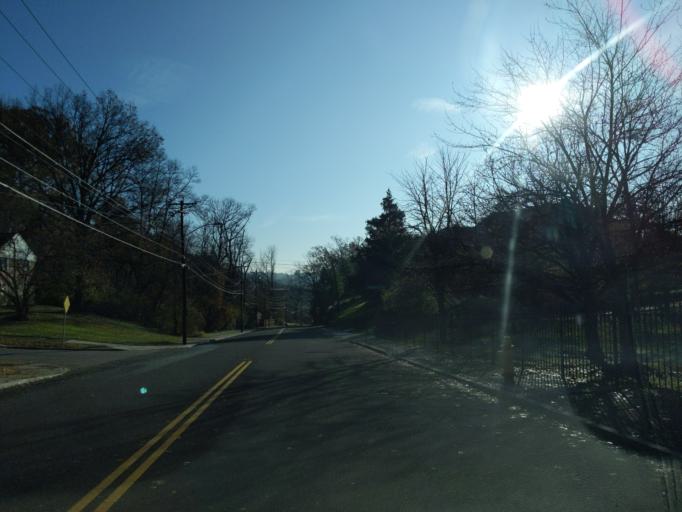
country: US
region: Kentucky
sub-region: Campbell County
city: Dayton
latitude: 39.1263
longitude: -84.4668
